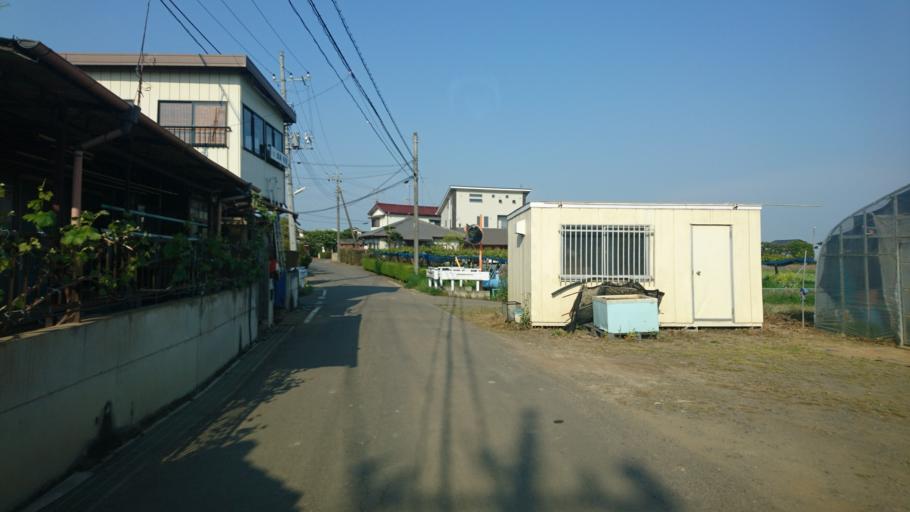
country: JP
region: Ibaraki
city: Yuki
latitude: 36.2494
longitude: 139.9198
